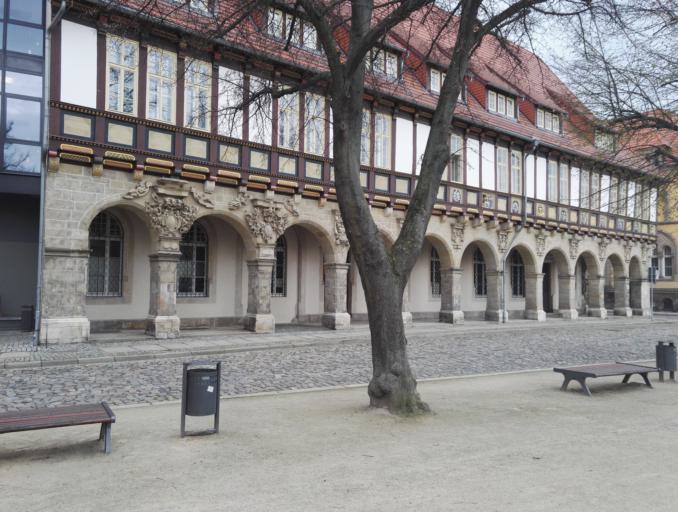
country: DE
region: Saxony-Anhalt
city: Halberstadt
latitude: 51.8958
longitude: 11.0473
